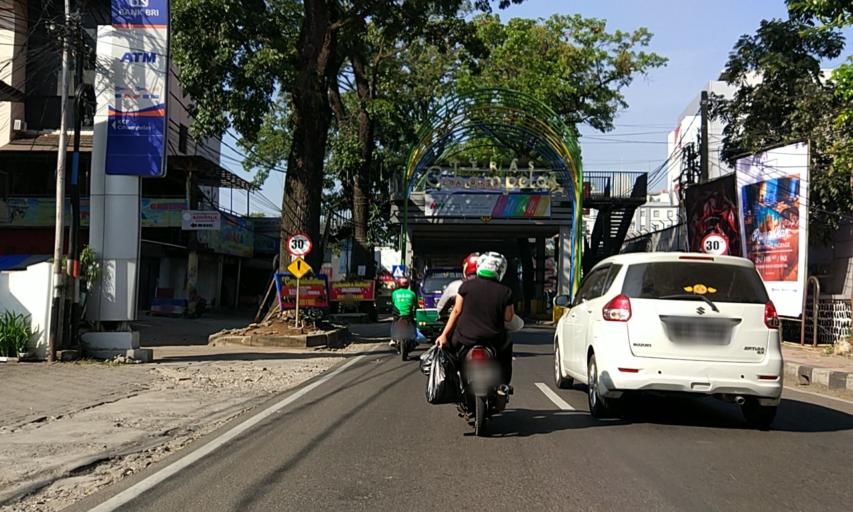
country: ID
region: West Java
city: Bandung
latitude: -6.8926
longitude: 107.6042
